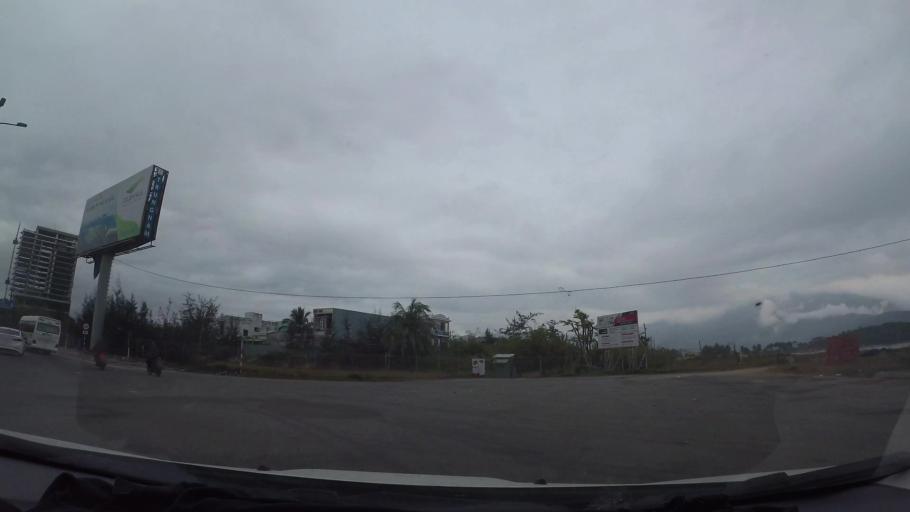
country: VN
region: Da Nang
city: Lien Chieu
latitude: 16.1104
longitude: 108.1323
